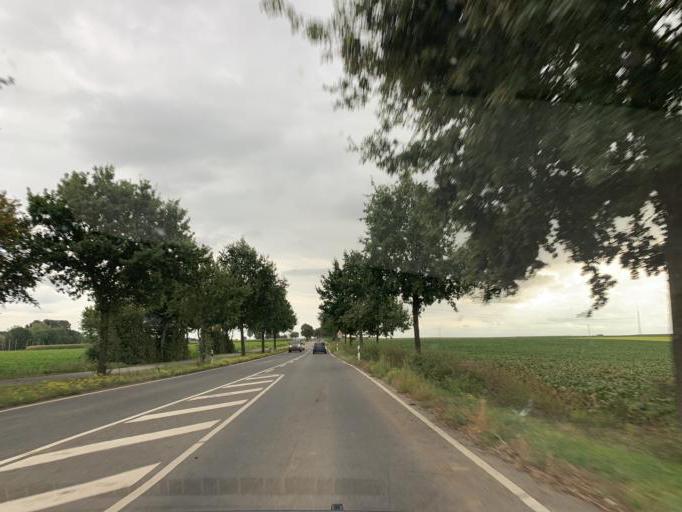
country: DE
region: North Rhine-Westphalia
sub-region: Regierungsbezirk Koln
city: Linnich
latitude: 50.9959
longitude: 6.2536
